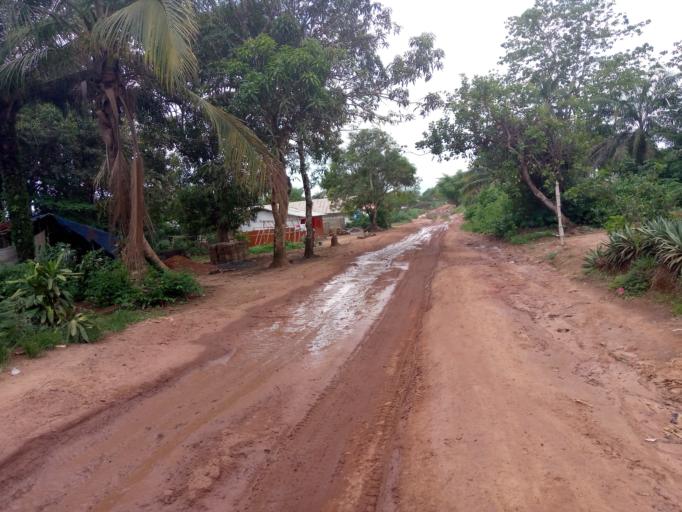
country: SL
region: Western Area
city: Waterloo
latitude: 8.3891
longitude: -12.9495
